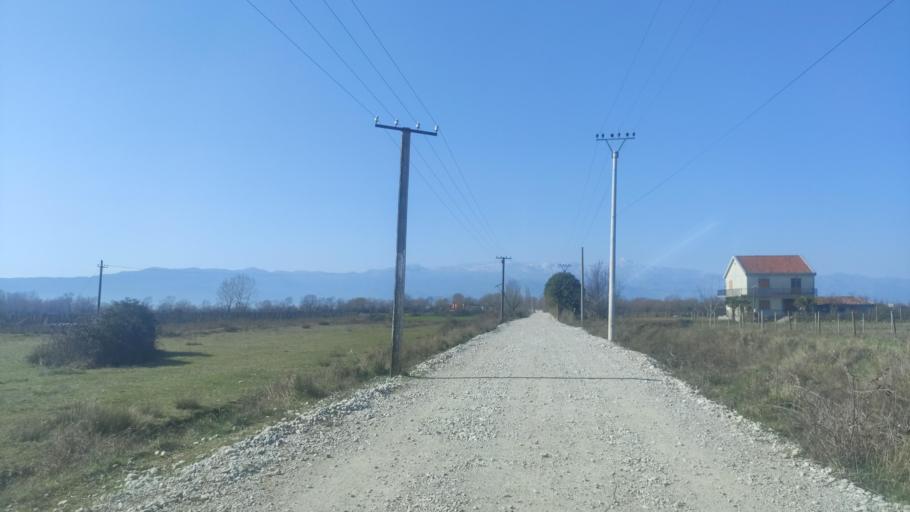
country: AL
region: Shkoder
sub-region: Rrethi i Malesia e Madhe
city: Grude-Fushe
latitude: 42.1595
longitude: 19.4516
